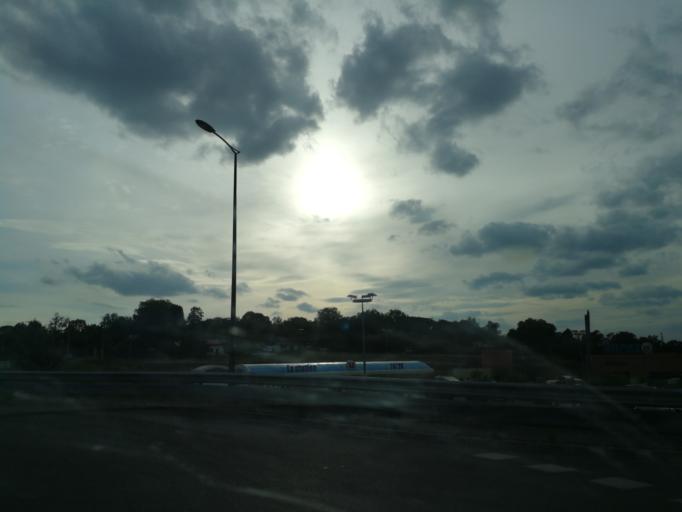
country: FR
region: Midi-Pyrenees
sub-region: Departement de la Haute-Garonne
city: Flourens
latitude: 43.5875
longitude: 1.5799
